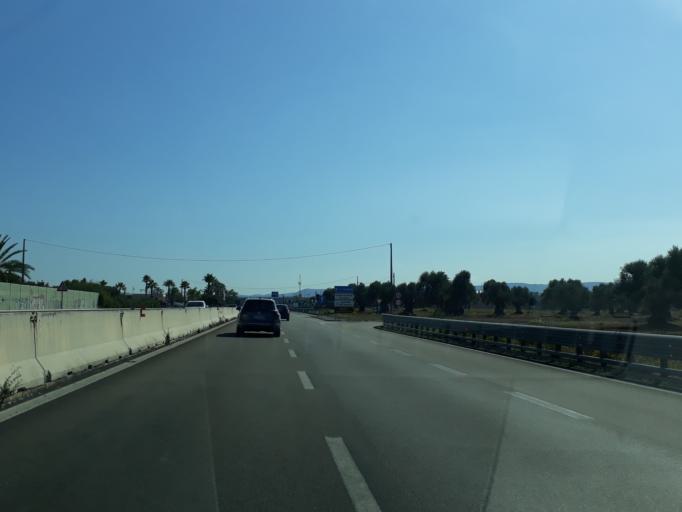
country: IT
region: Apulia
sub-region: Provincia di Brindisi
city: Fasano
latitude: 40.8552
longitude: 17.3528
